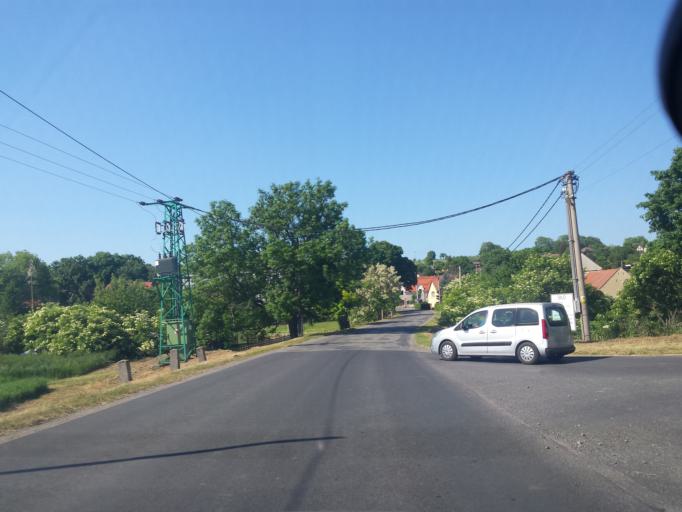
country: CZ
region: Central Bohemia
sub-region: Okres Melnik
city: Melnik
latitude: 50.4039
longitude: 14.5198
